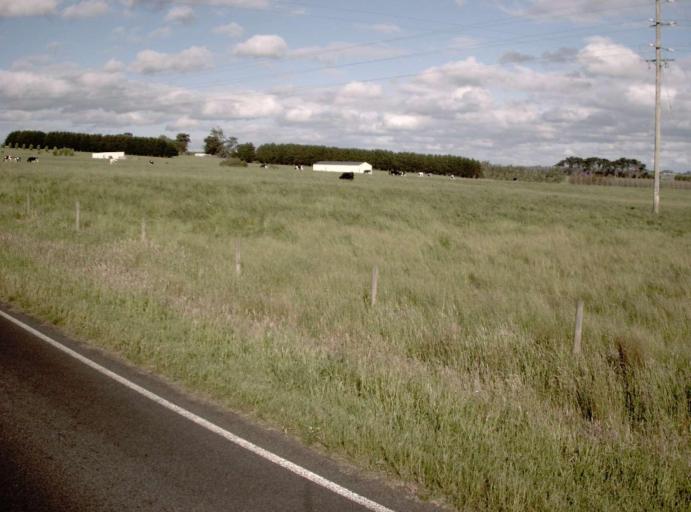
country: AU
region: Victoria
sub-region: Bass Coast
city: North Wonthaggi
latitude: -38.5011
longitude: 145.9177
